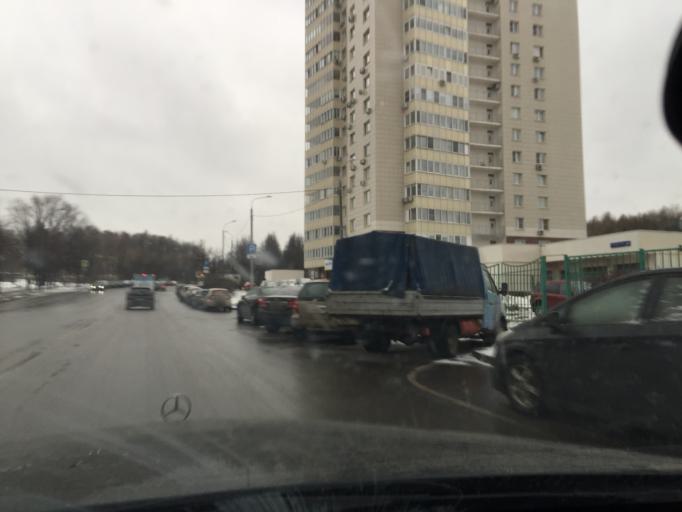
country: RU
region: Moscow
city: Troparevo
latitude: 55.6479
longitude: 37.4692
